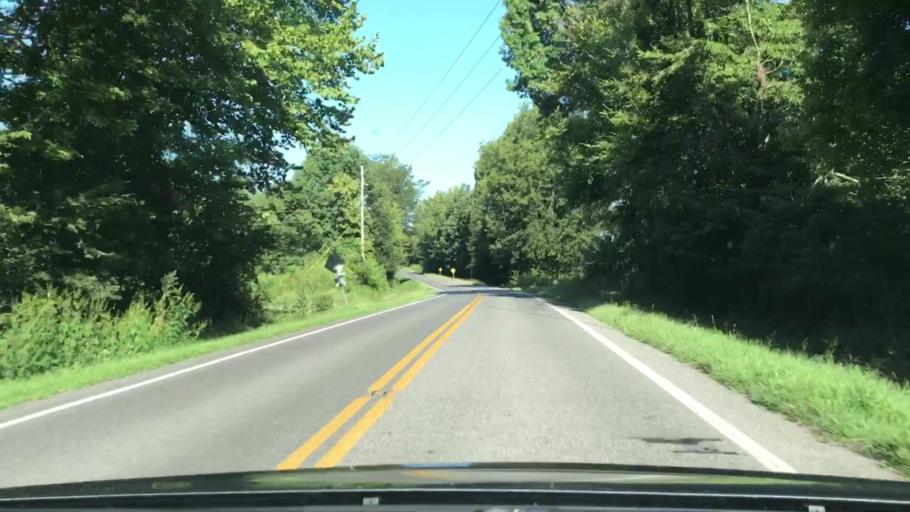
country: US
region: Kentucky
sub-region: Graves County
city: Mayfield
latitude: 36.7803
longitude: -88.5217
